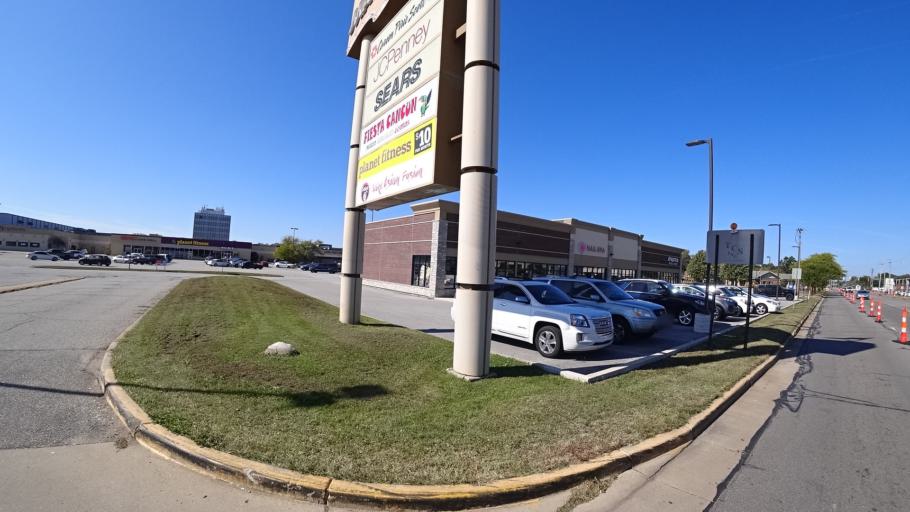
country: US
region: Indiana
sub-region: LaPorte County
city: Michigan City
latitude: 41.6821
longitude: -86.8941
